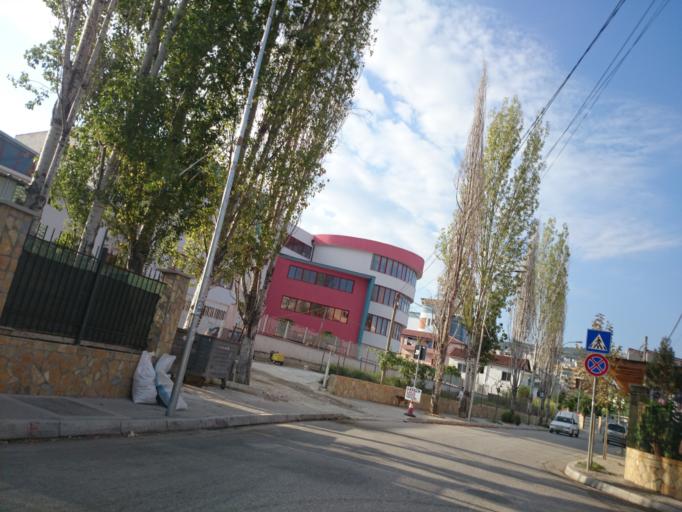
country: AL
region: Tirane
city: Tirana
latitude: 41.3173
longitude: 19.8022
